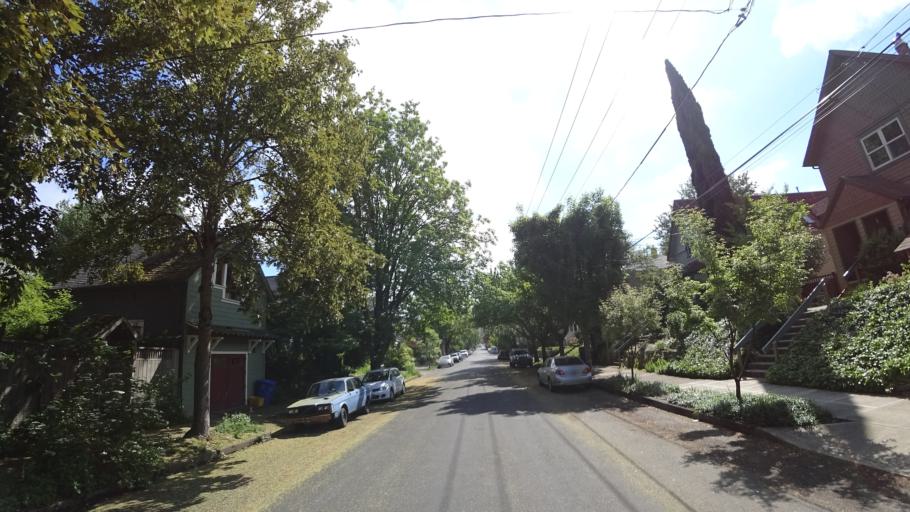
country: US
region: Oregon
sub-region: Multnomah County
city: Portland
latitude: 45.5150
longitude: -122.6335
